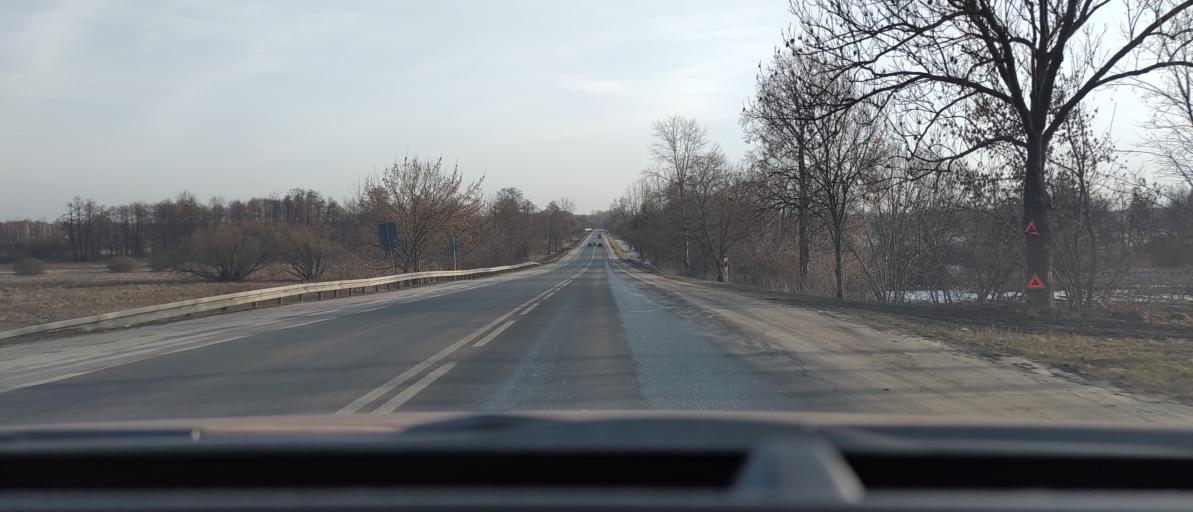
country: PL
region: Masovian Voivodeship
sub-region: Powiat bialobrzeski
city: Promna
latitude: 51.6713
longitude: 20.9445
